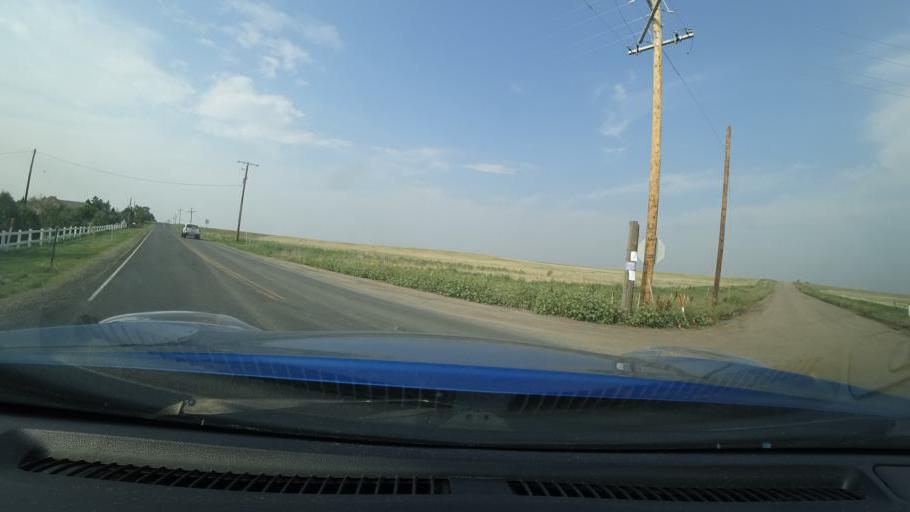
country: US
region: Colorado
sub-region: Adams County
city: Aurora
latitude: 39.7256
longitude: -104.7349
